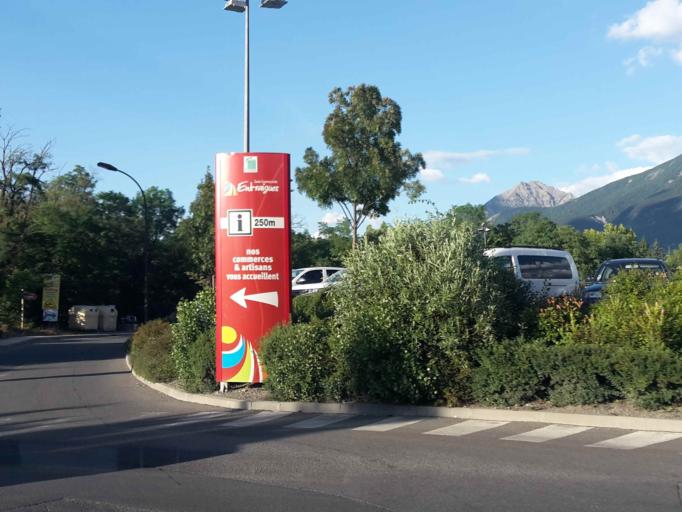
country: FR
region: Provence-Alpes-Cote d'Azur
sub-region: Departement des Hautes-Alpes
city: Embrun
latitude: 44.5506
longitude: 6.4863
